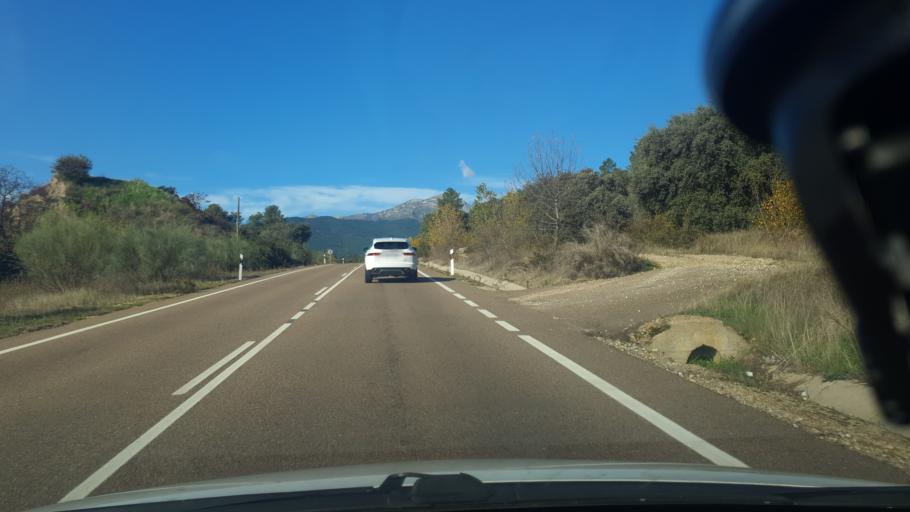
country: ES
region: Castille and Leon
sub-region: Provincia de Avila
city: Arenas de San Pedro
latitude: 40.1892
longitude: -5.0674
